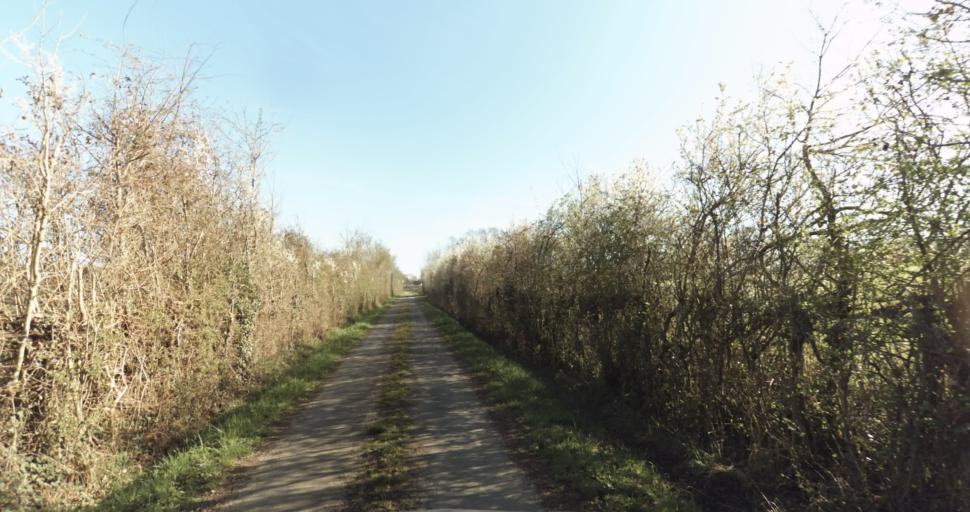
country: FR
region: Lower Normandy
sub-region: Departement du Calvados
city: Saint-Pierre-sur-Dives
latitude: 49.0447
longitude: 0.0509
